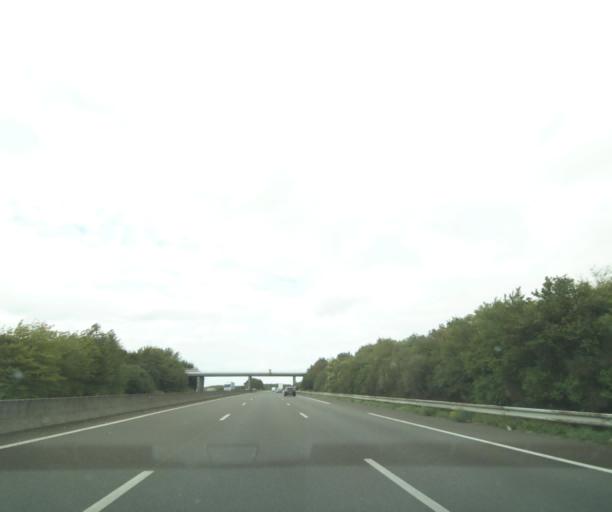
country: FR
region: Ile-de-France
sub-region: Departement de l'Essonne
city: Corbreuse
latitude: 48.5018
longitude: 1.9078
